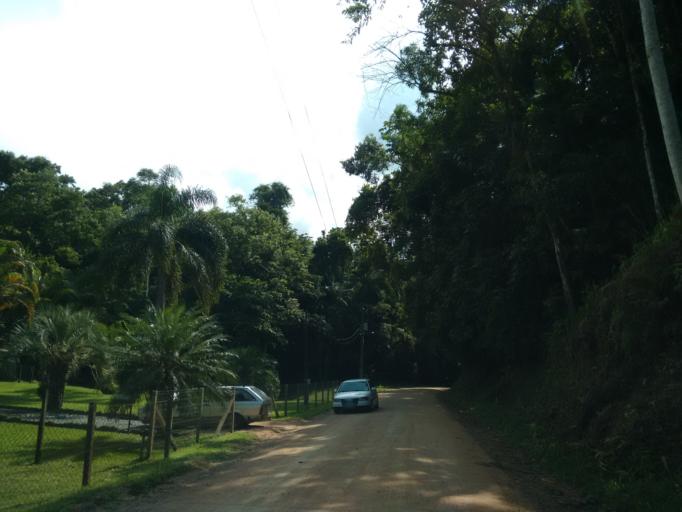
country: BR
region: Santa Catarina
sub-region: Pomerode
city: Pomerode
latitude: -26.7879
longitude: -49.1383
